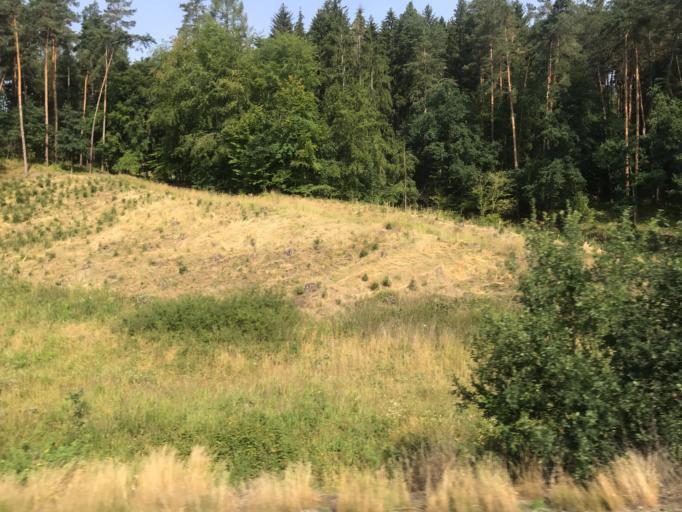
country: CZ
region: Central Bohemia
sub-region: Okres Benesov
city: Cercany
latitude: 49.8235
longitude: 14.7018
